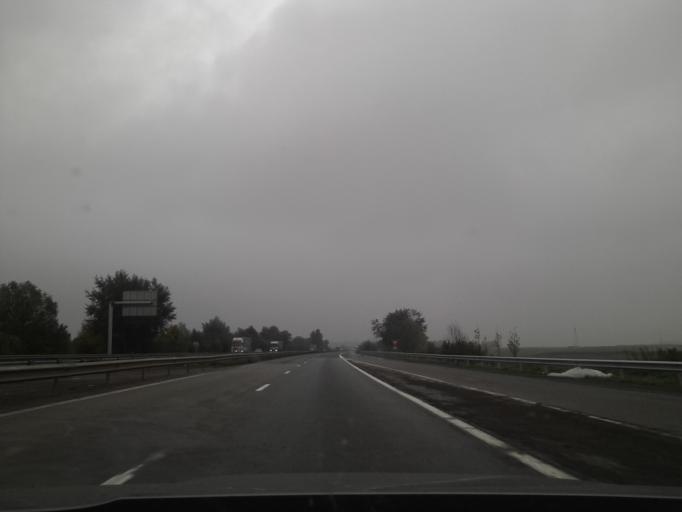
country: FR
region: Nord-Pas-de-Calais
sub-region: Departement du Nord
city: Onnaing
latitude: 50.3769
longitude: 3.6070
